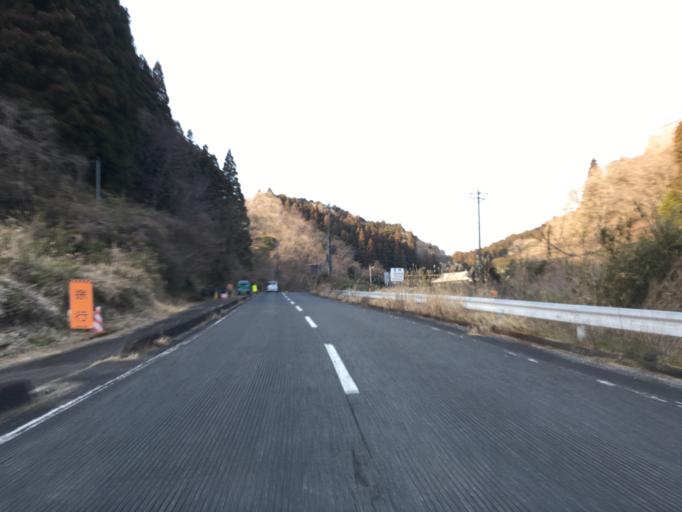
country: JP
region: Ibaraki
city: Daigo
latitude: 36.7433
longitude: 140.4541
